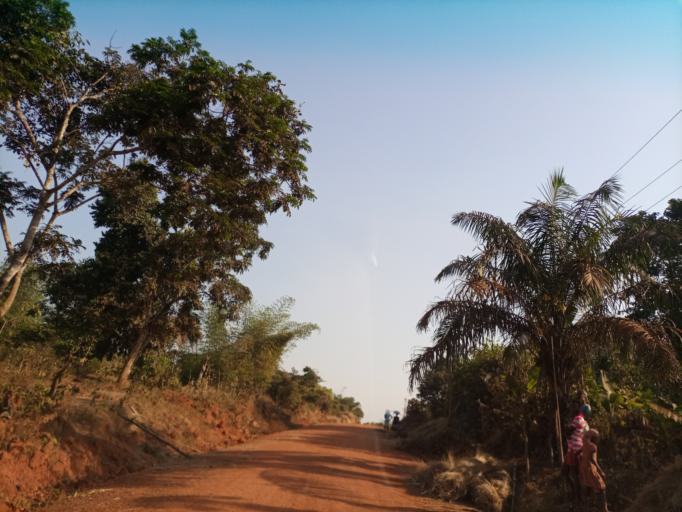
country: NG
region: Enugu
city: Opi
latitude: 6.7648
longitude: 7.3959
